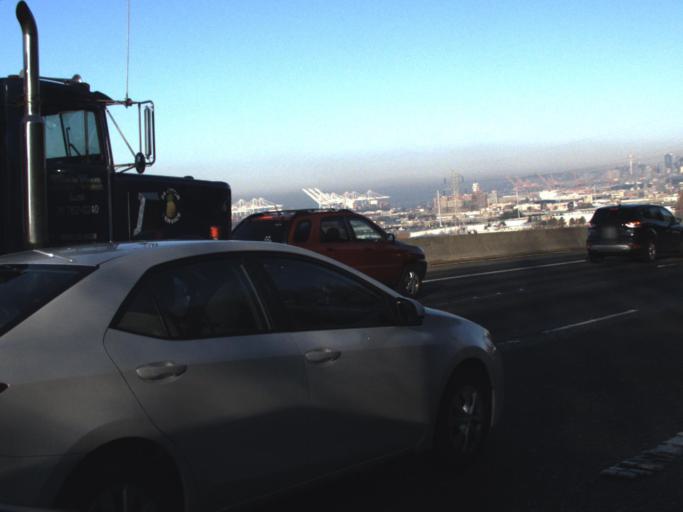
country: US
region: Washington
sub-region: King County
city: Seattle
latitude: 47.5614
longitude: -122.3215
